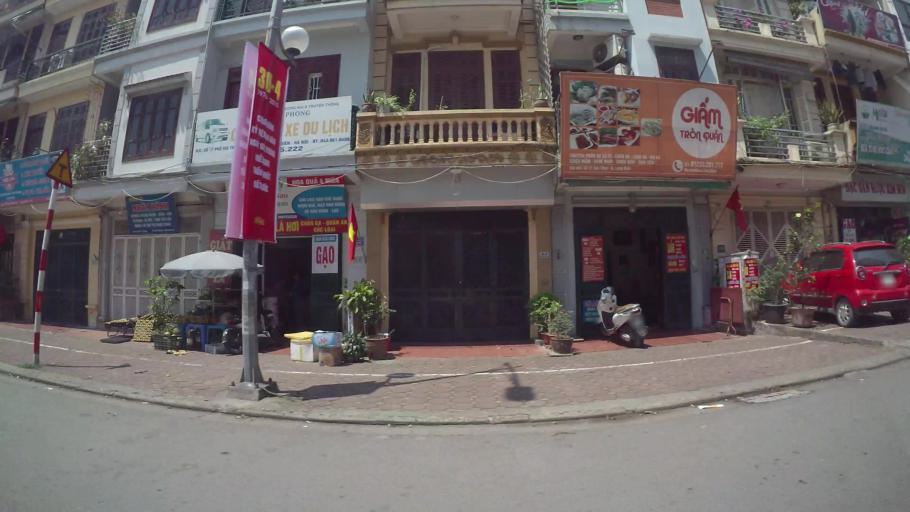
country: VN
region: Ha Noi
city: Hoan Kiem
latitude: 21.0478
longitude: 105.8855
